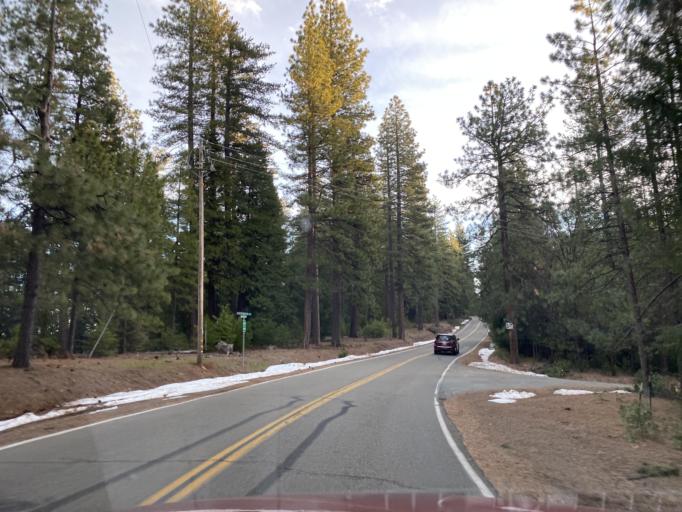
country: US
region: California
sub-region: Amador County
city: Pioneer
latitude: 38.5025
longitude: -120.5375
